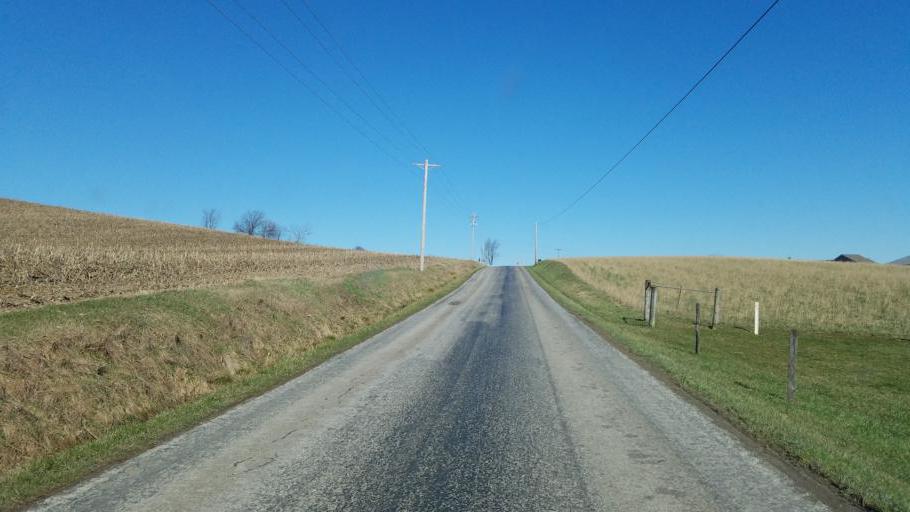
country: US
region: Ohio
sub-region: Wayne County
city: Dalton
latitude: 40.6714
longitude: -81.7304
